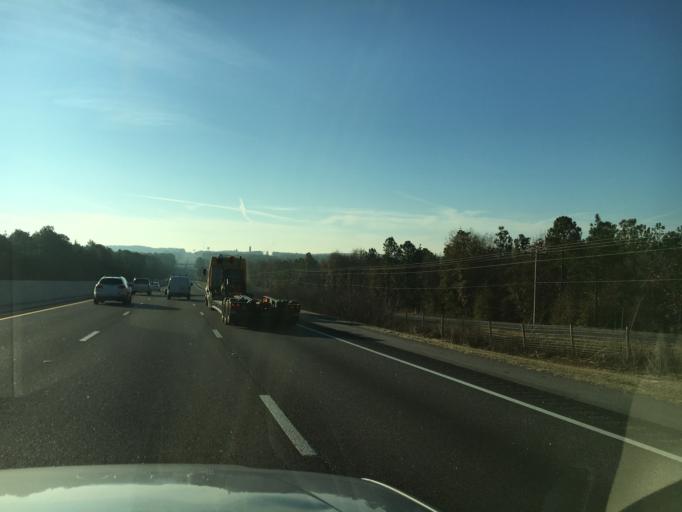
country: US
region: South Carolina
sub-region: Lexington County
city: Gaston
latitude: 33.8600
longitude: -81.0303
